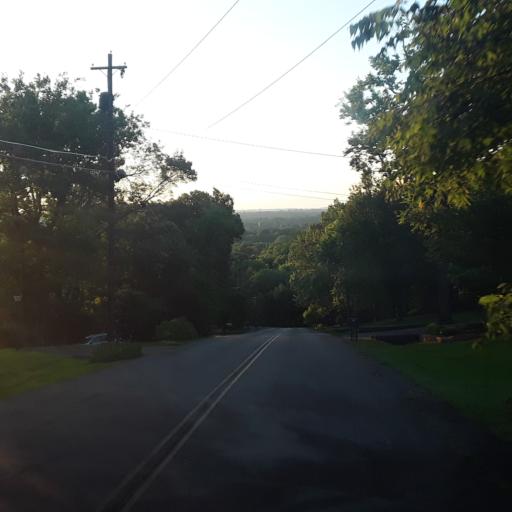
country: US
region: Tennessee
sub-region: Davidson County
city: Oak Hill
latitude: 36.0679
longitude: -86.7793
